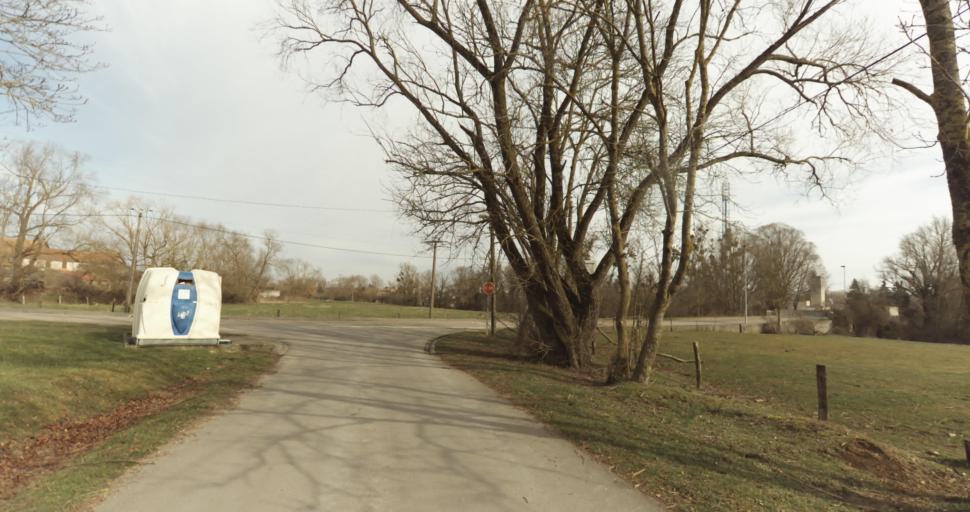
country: FR
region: Lorraine
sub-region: Departement de Meurthe-et-Moselle
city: Jarny
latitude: 49.1420
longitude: 5.8746
